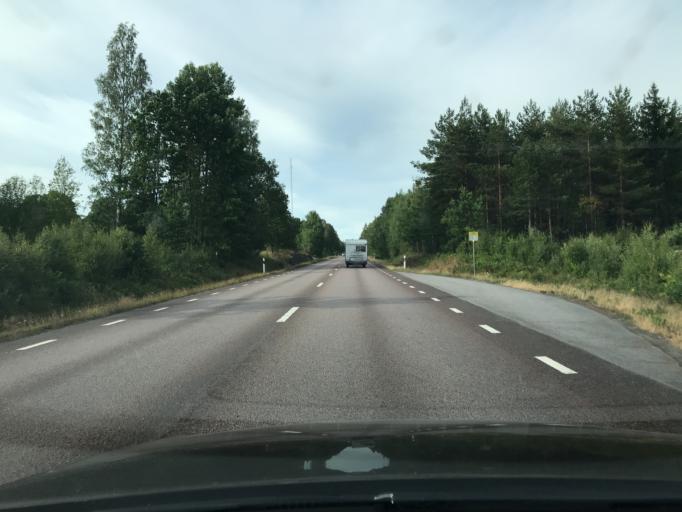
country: SE
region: Kalmar
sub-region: Hultsfreds Kommun
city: Hultsfred
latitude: 57.4551
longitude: 15.8362
